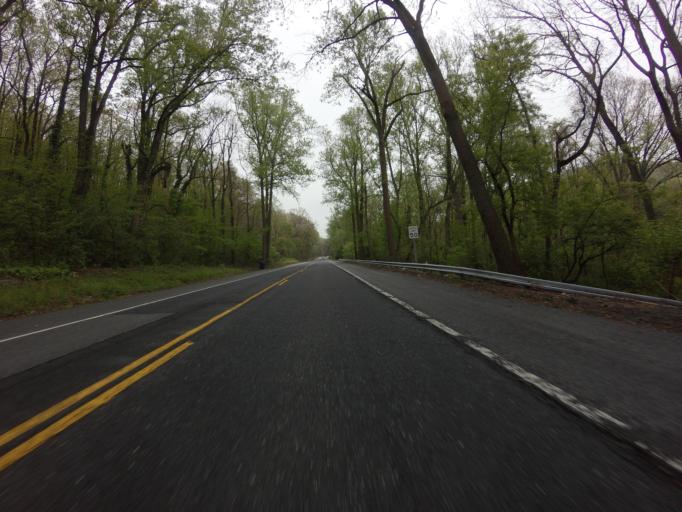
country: US
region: Maryland
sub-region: Frederick County
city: Braddock Heights
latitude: 39.4513
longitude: -77.4977
